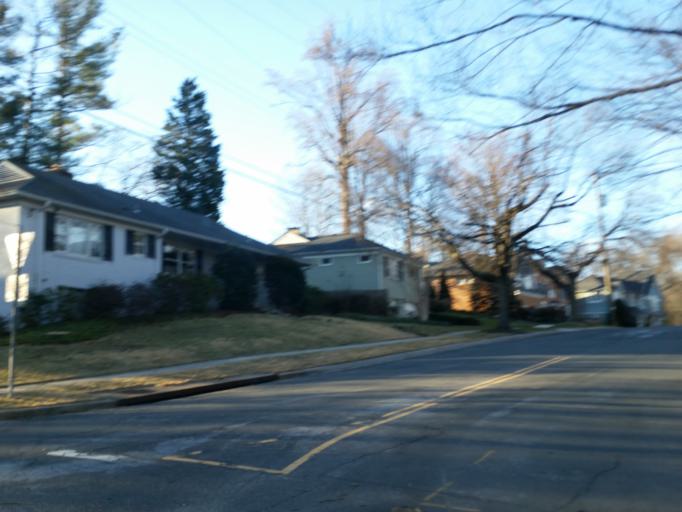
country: US
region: Maryland
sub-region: Montgomery County
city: Brookmont
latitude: 38.9585
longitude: -77.1150
